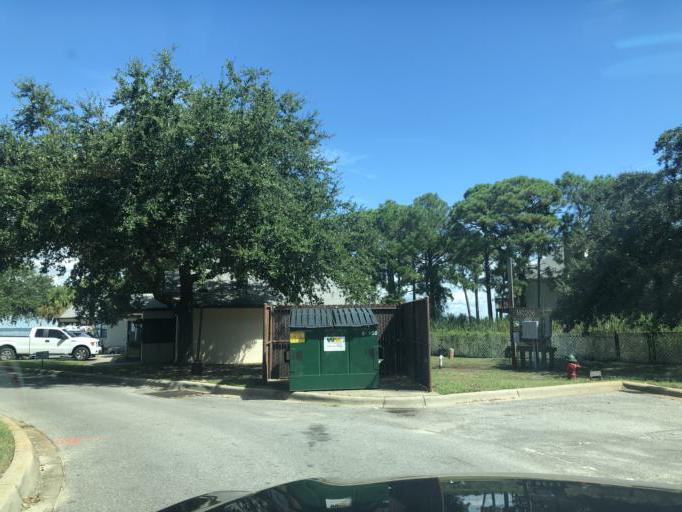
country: US
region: Florida
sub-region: Okaloosa County
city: Destin
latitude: 30.4120
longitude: -86.4983
